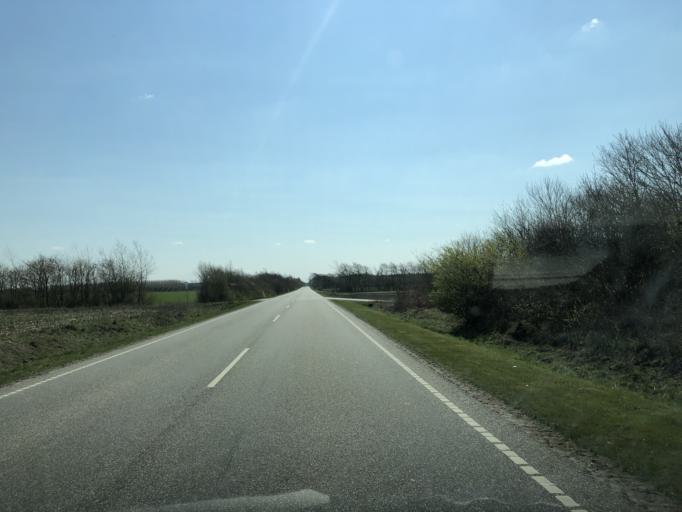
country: DK
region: Central Jutland
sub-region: Holstebro Kommune
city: Ulfborg
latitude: 56.3896
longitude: 8.3227
